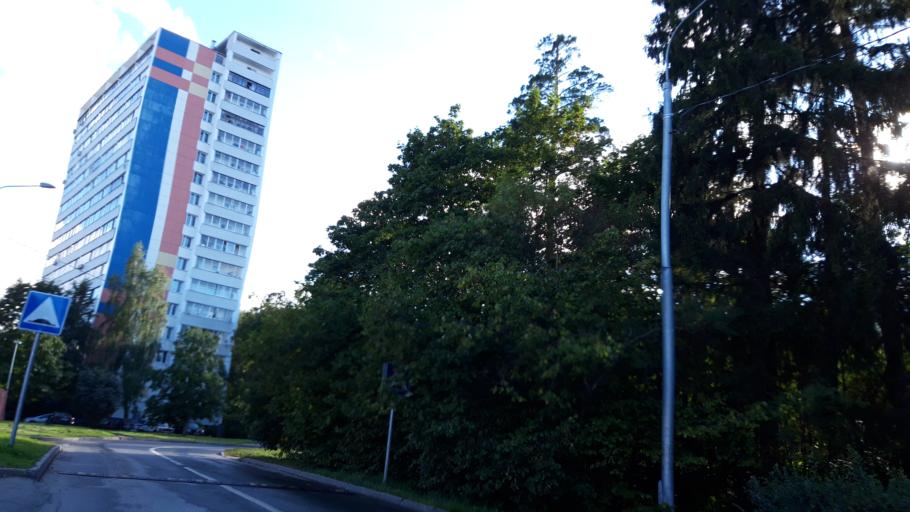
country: RU
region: Moscow
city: Zelenograd
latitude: 55.9876
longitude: 37.1877
